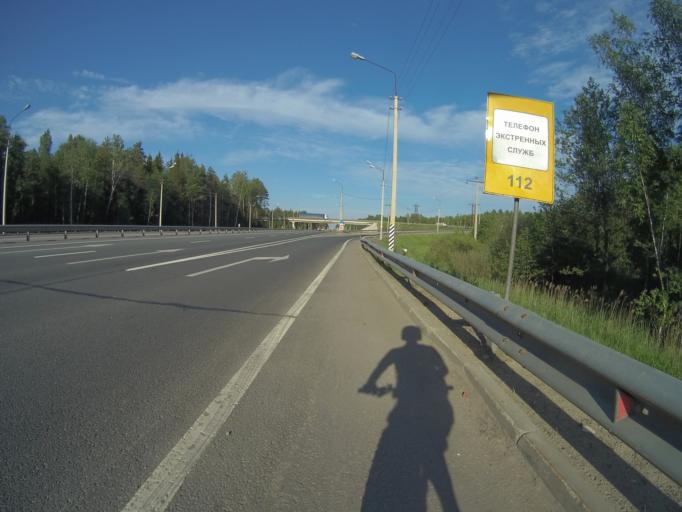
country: RU
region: Vladimir
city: Kameshkovo
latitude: 56.1940
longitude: 40.9477
